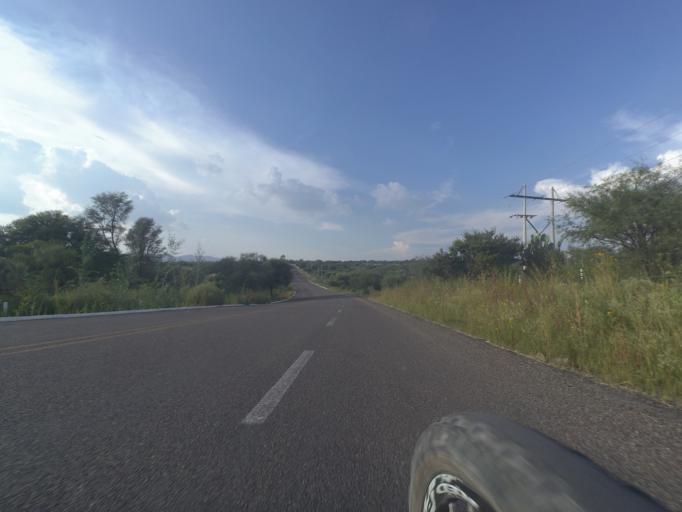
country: MX
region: Aguascalientes
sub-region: Aguascalientes
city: Penuelas (El Cienegal)
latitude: 21.7590
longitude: -102.3505
